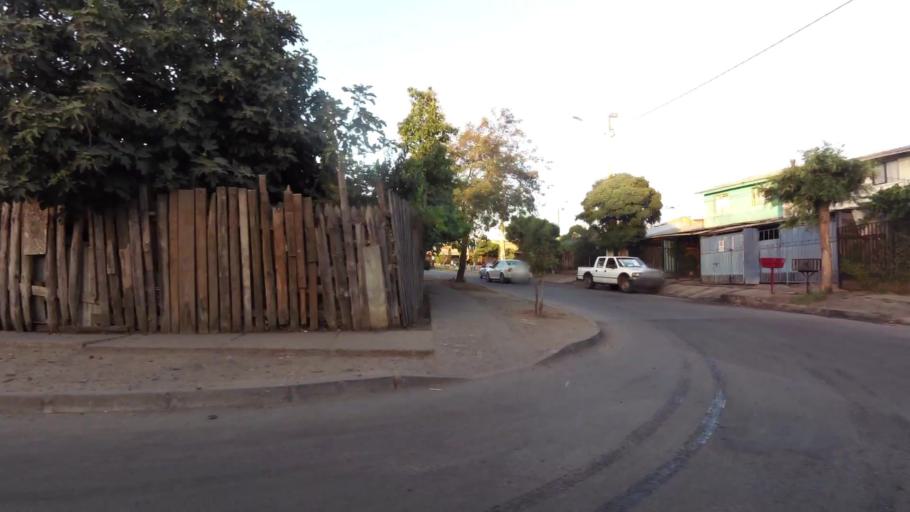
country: CL
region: Maule
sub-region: Provincia de Talca
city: Talca
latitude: -35.4480
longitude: -71.6353
